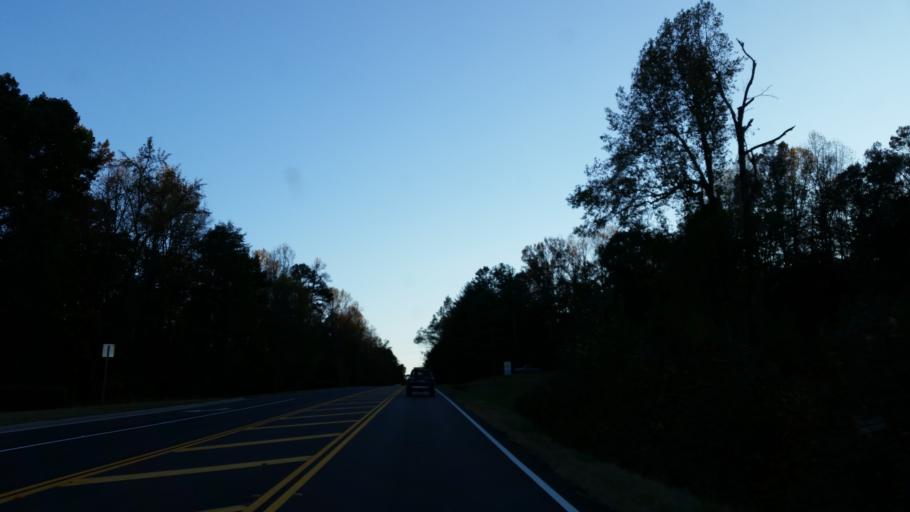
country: US
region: Georgia
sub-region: Lumpkin County
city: Dahlonega
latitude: 34.4960
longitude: -83.9705
